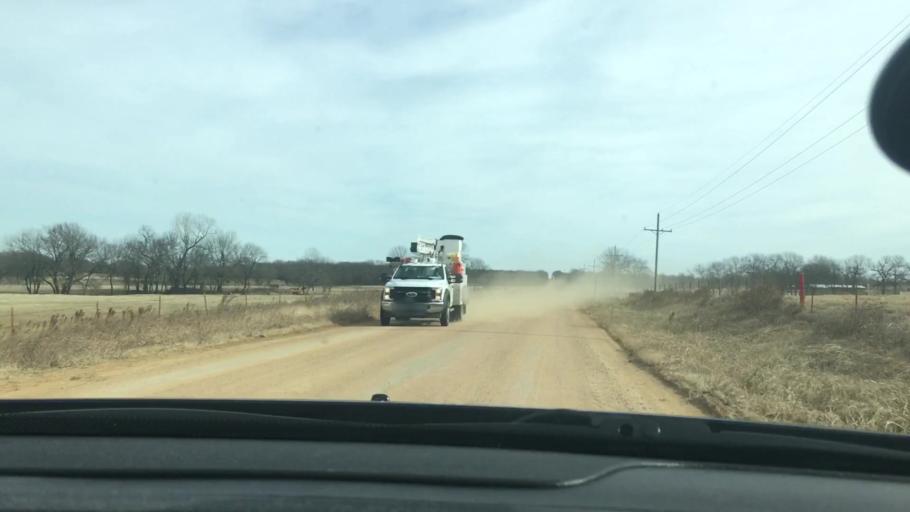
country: US
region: Oklahoma
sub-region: Murray County
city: Sulphur
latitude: 34.4048
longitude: -96.9159
